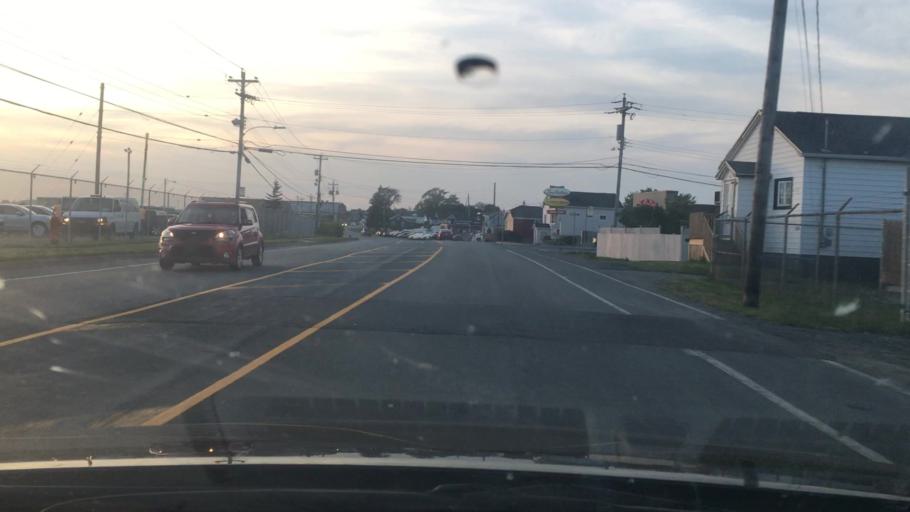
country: CA
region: Nova Scotia
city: Cole Harbour
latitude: 44.6230
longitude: -63.5096
